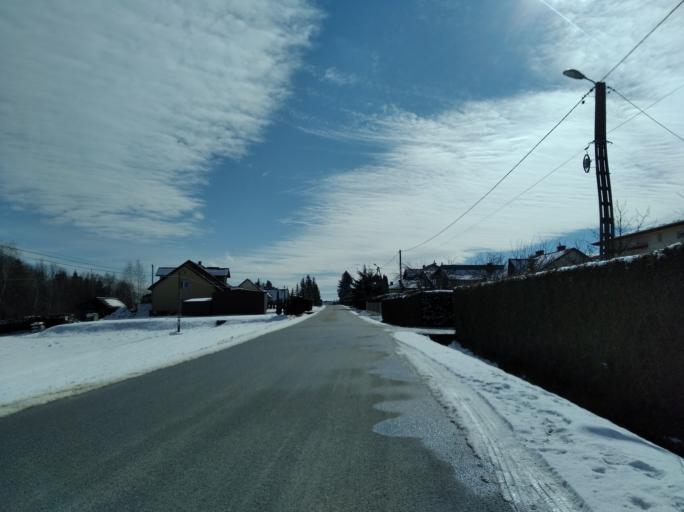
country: PL
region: Subcarpathian Voivodeship
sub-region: Powiat brzozowski
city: Jablonica Polska
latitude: 49.7257
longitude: 21.9022
